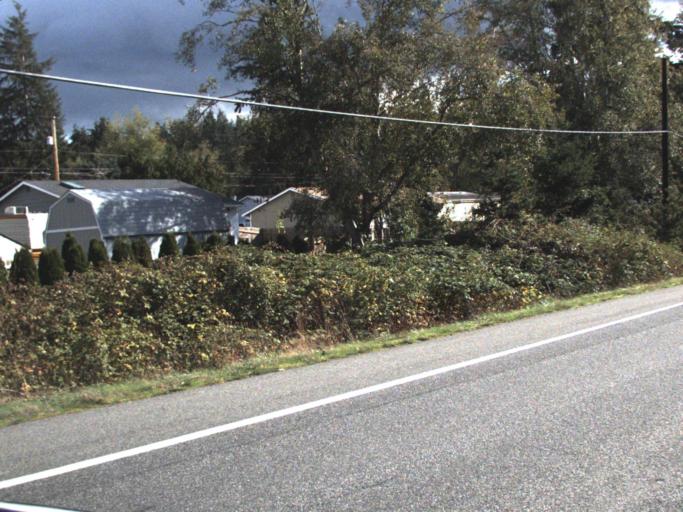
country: US
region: Washington
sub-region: Island County
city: Ault Field
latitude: 48.3650
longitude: -122.6500
